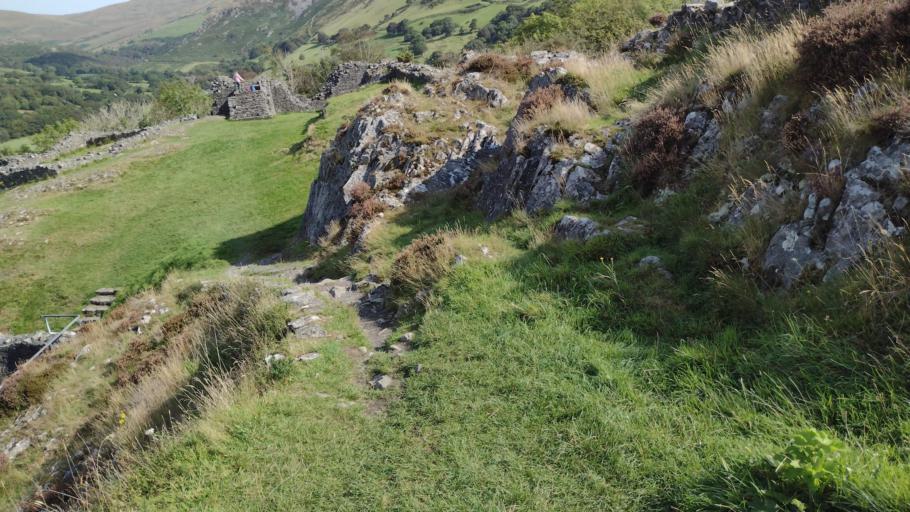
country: GB
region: Wales
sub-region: Gwynedd
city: Barmouth
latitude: 52.6581
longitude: -3.9713
